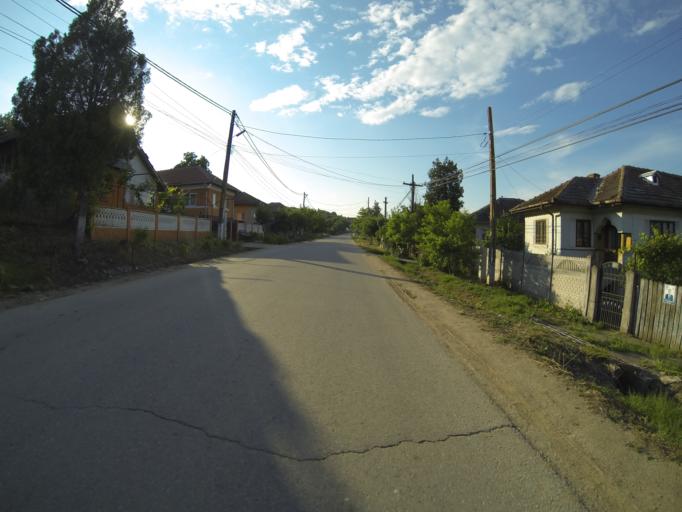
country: RO
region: Dolj
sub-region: Comuna Tuglui
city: Tuglui
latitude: 44.1999
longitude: 23.8005
